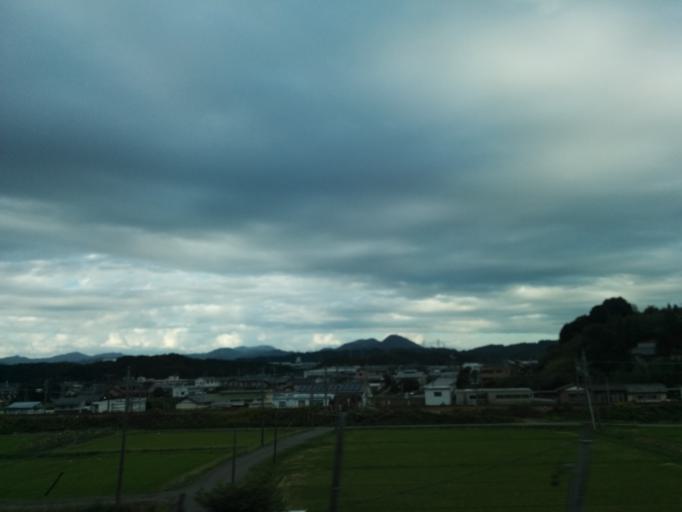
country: JP
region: Shizuoka
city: Kakegawa
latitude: 34.7742
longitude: 138.0410
